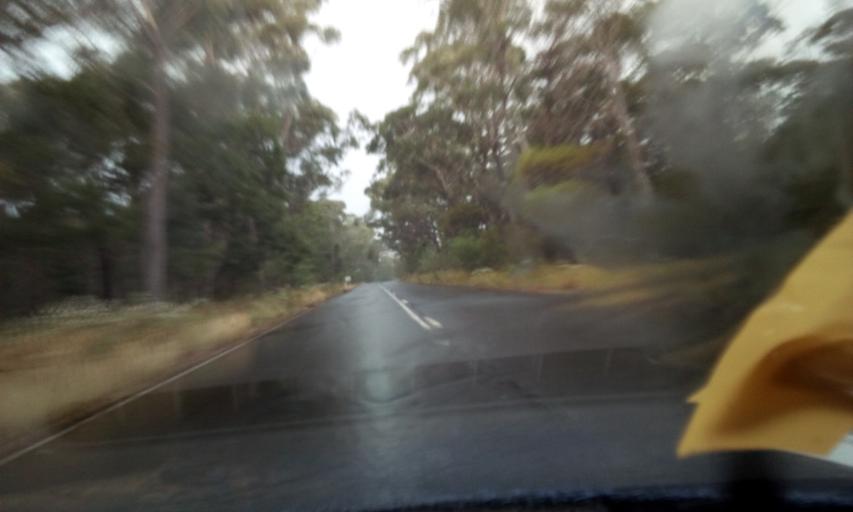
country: AU
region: New South Wales
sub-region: Wollongong
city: Mount Keira
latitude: -34.3854
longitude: 150.8385
